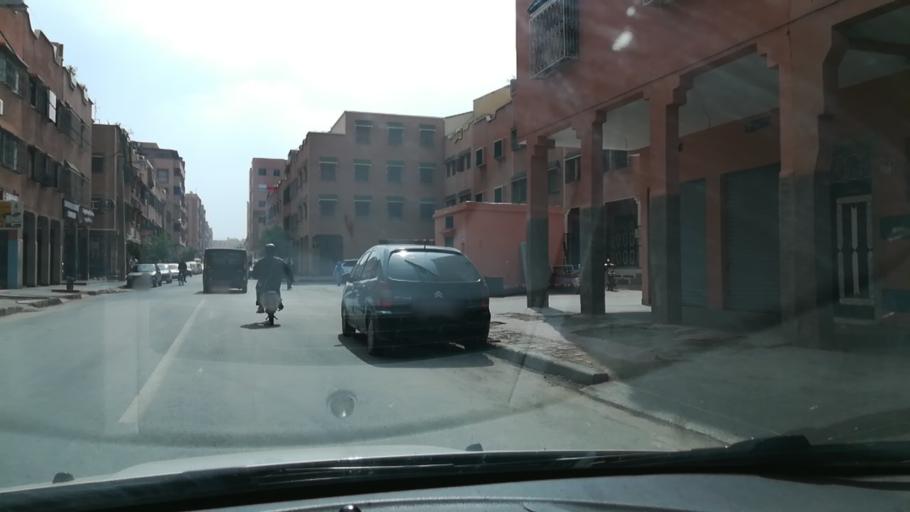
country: MA
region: Marrakech-Tensift-Al Haouz
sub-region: Marrakech
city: Marrakesh
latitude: 31.6294
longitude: -8.0644
